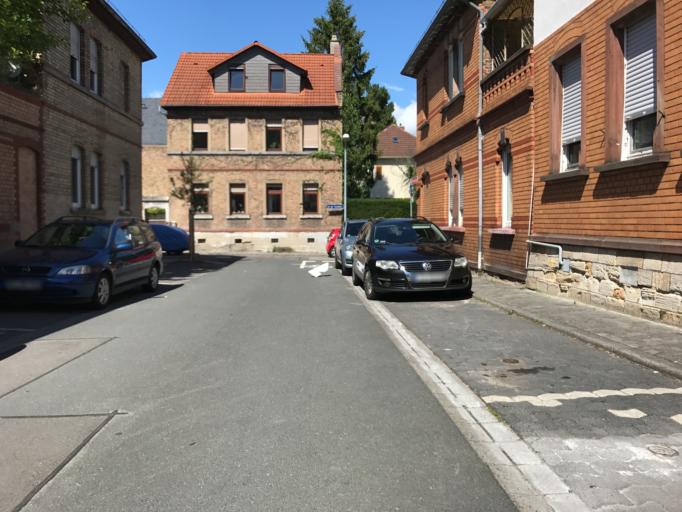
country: DE
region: Rheinland-Pfalz
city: Mainz
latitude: 49.9805
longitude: 8.2990
